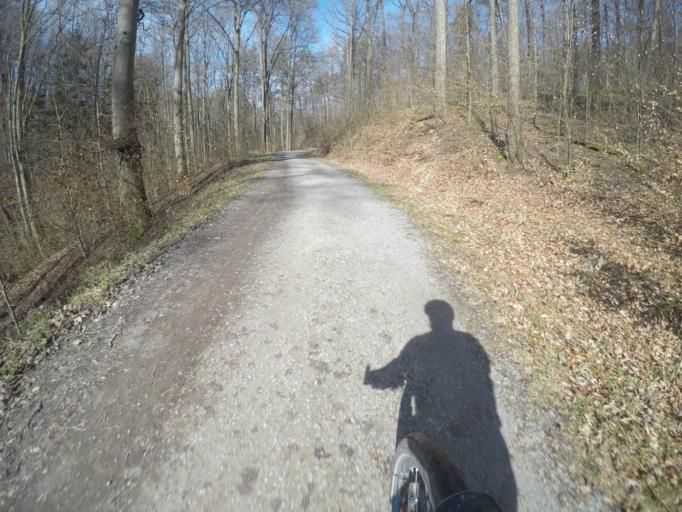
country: DE
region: Baden-Wuerttemberg
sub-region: Regierungsbezirk Stuttgart
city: Korntal
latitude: 48.7904
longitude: 9.1085
